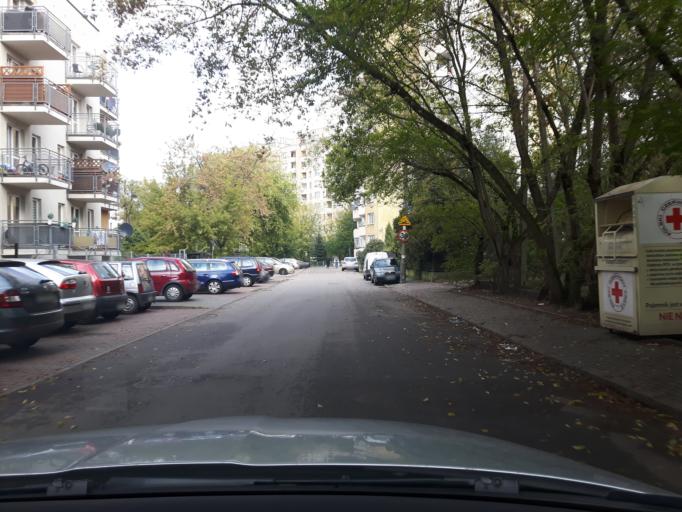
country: PL
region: Masovian Voivodeship
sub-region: Warszawa
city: Praga Polnoc
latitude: 52.2671
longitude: 21.0457
